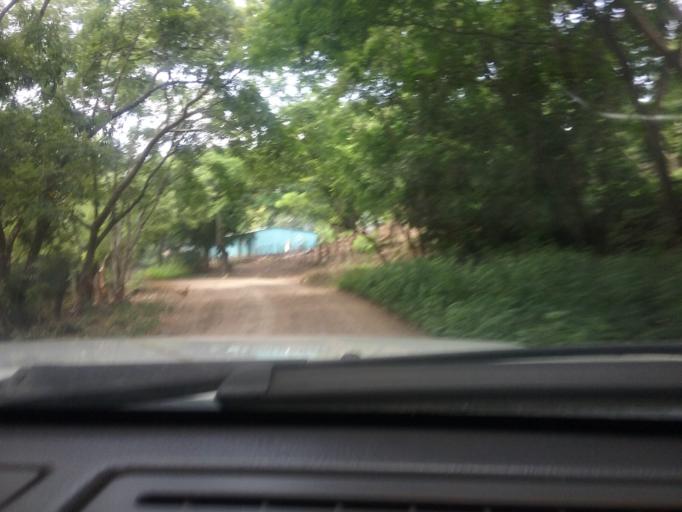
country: NI
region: Matagalpa
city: Terrabona
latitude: 12.7035
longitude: -85.9513
